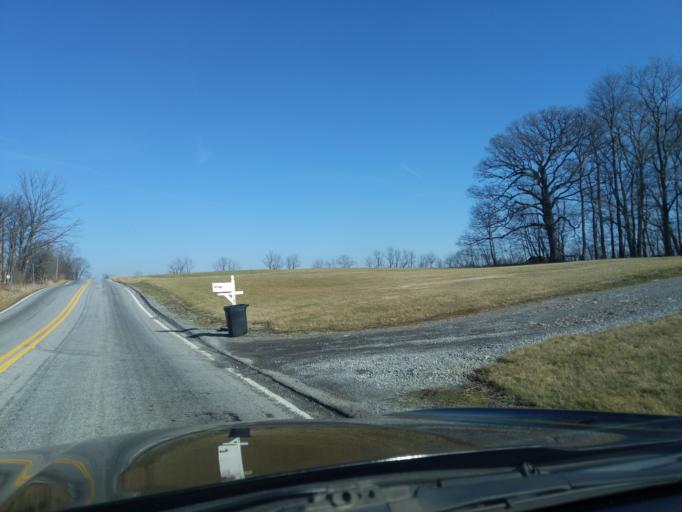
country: US
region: Pennsylvania
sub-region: Blair County
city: Tipton
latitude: 40.6096
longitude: -78.2615
